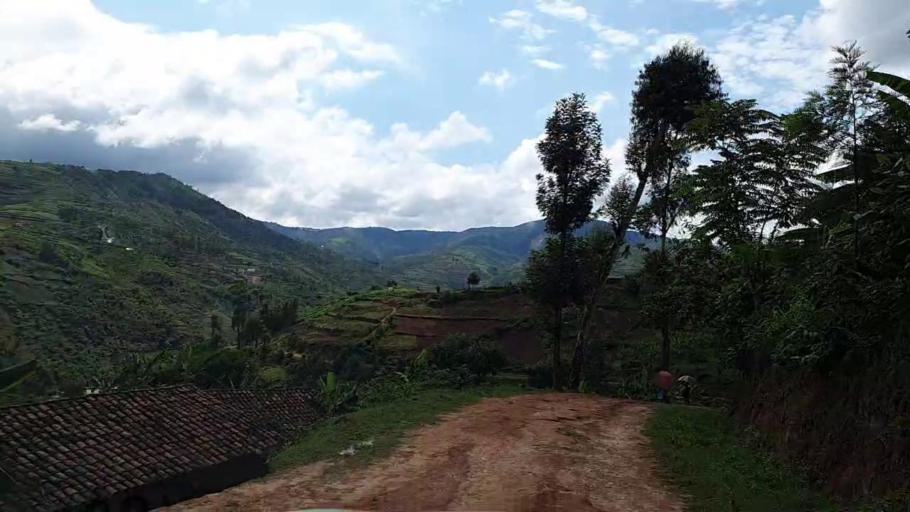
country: RW
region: Southern Province
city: Gikongoro
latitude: -2.3605
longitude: 29.5451
